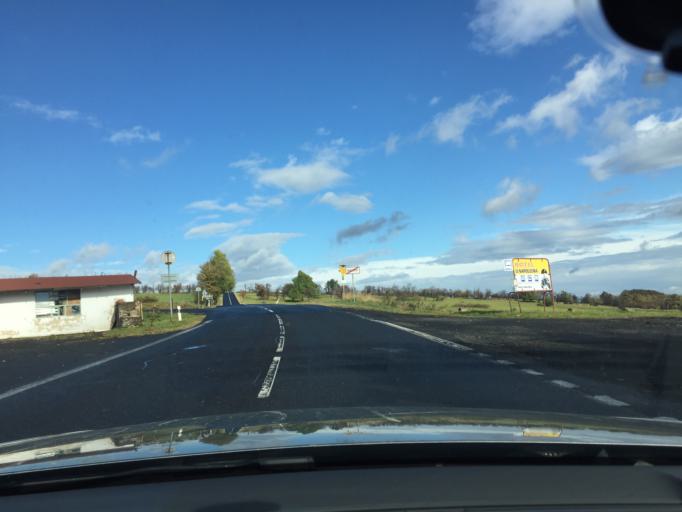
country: CZ
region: Ustecky
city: Chlumec
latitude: 50.7454
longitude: 13.9770
